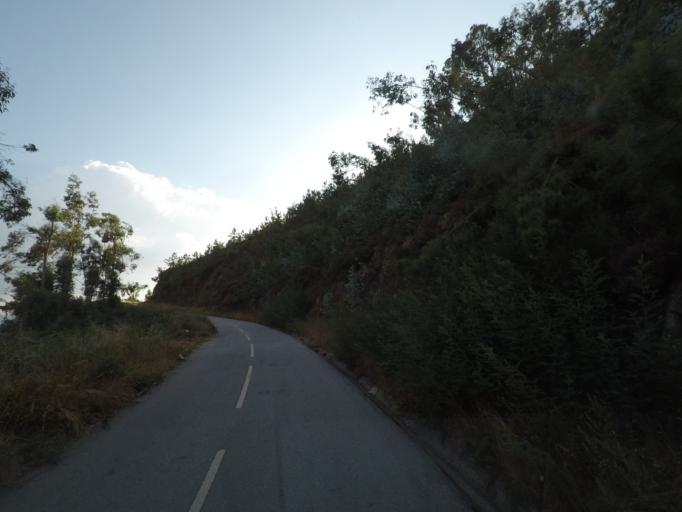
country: PT
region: Vila Real
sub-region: Mesao Frio
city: Mesao Frio
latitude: 41.1652
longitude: -7.9109
